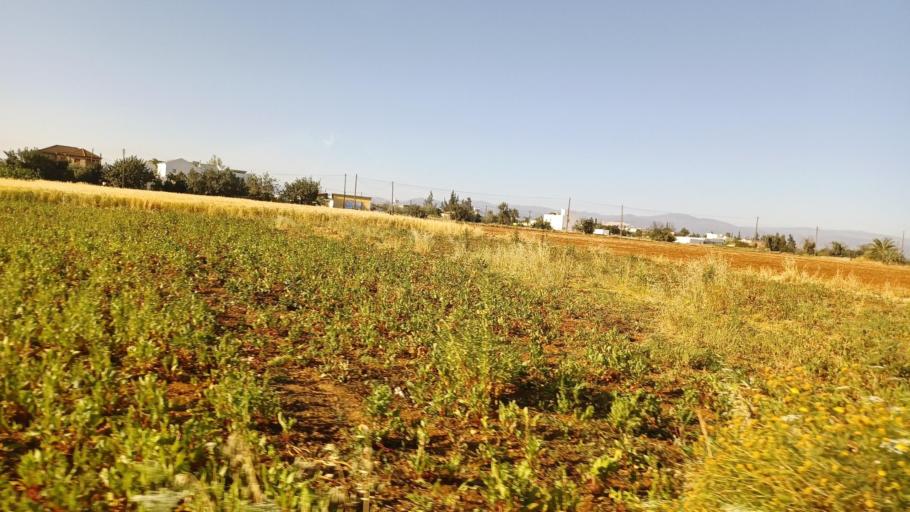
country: CY
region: Lefkosia
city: Kokkinotrimithia
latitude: 35.1507
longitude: 33.1876
